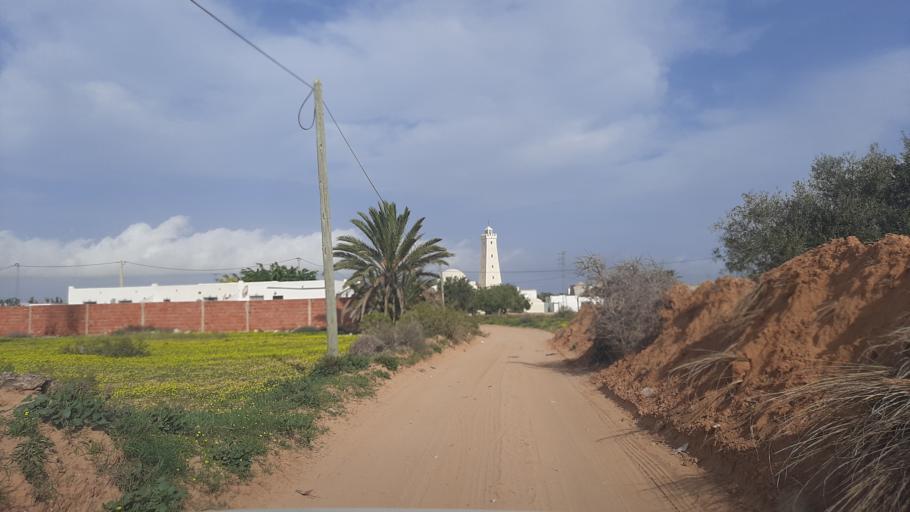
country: TN
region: Madanin
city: Midoun
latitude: 33.7969
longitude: 11.0293
